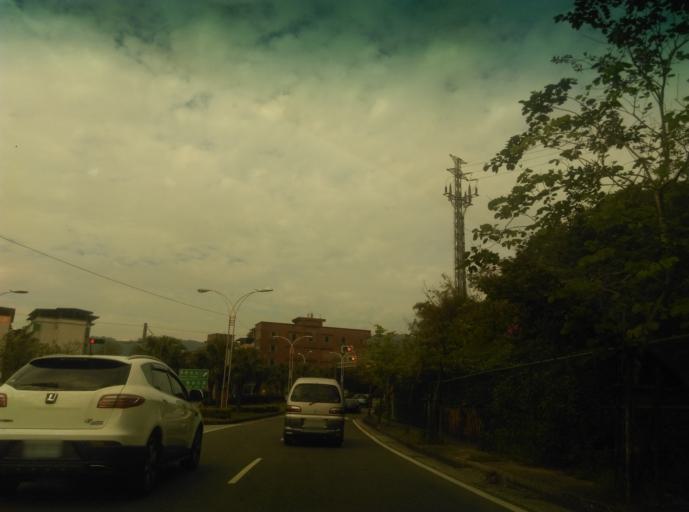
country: TW
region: Taiwan
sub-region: Keelung
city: Keelung
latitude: 25.1553
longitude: 121.6967
